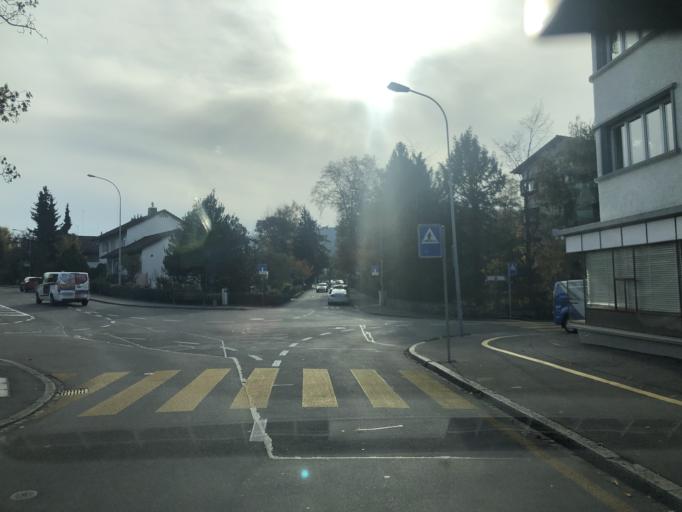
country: CH
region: Aargau
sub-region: Bezirk Baden
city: Wettingen
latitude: 47.4625
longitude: 8.3185
